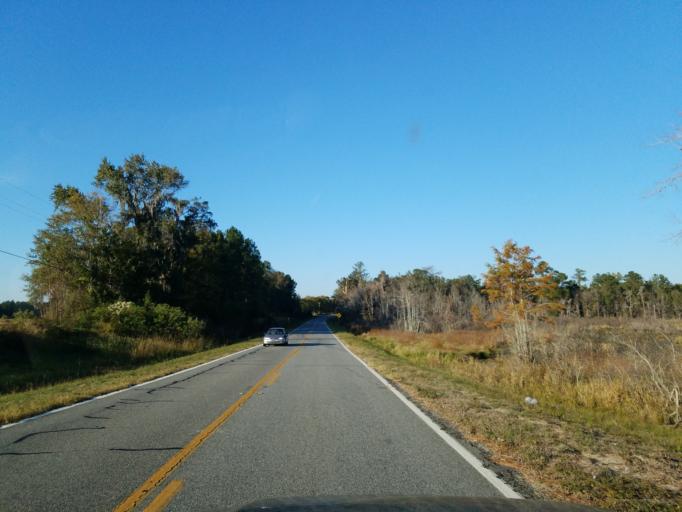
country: US
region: Georgia
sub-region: Lanier County
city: Lakeland
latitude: 30.9668
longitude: -83.0821
